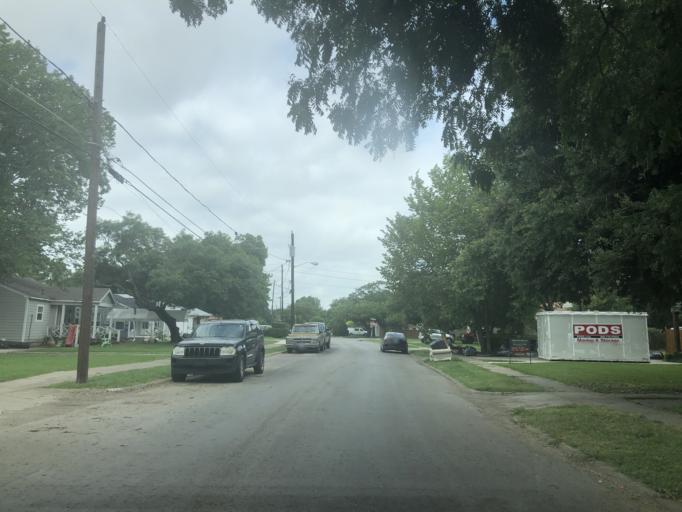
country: US
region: Texas
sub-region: Dallas County
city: University Park
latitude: 32.8663
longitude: -96.8549
